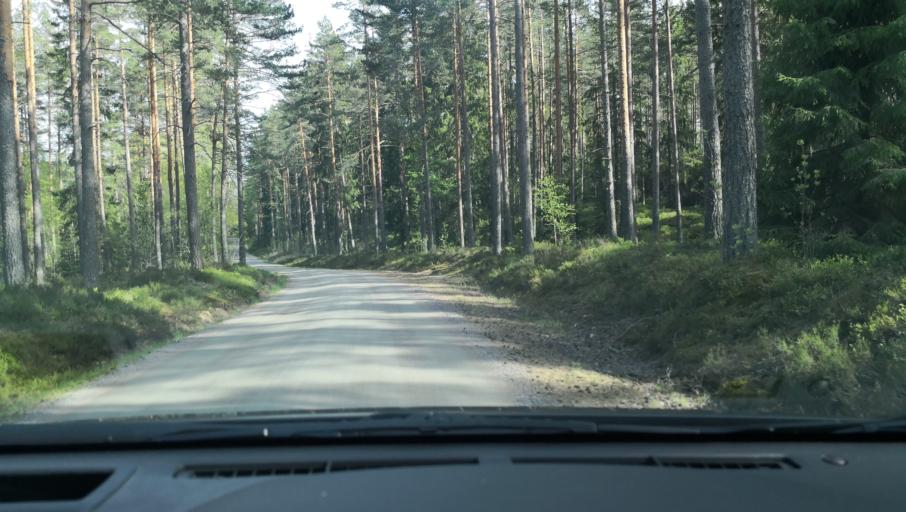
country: SE
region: OErebro
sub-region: Askersunds Kommun
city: Asbro
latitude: 59.0311
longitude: 15.0468
